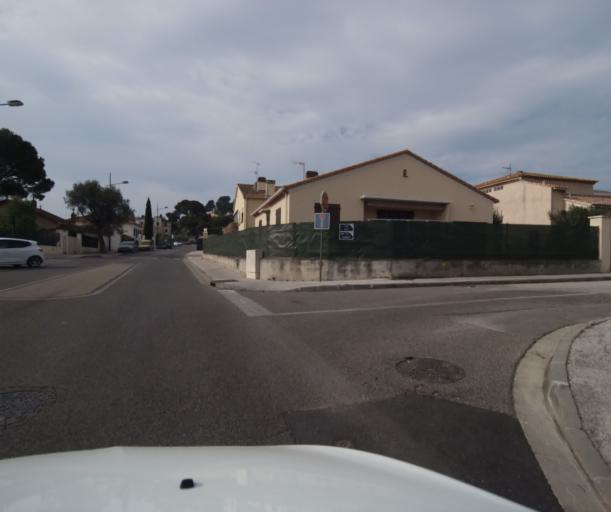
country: FR
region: Provence-Alpes-Cote d'Azur
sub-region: Departement du Var
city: Hyeres
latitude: 43.1090
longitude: 6.1219
